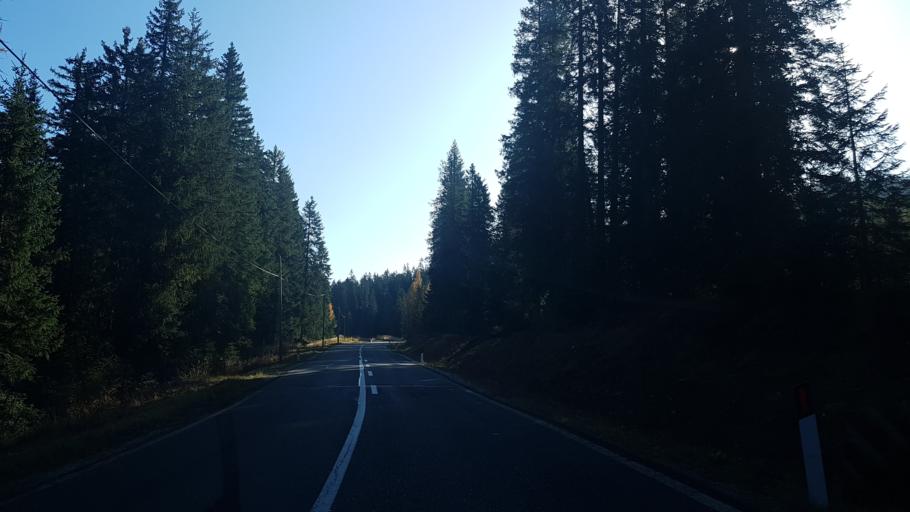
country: IT
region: Trentino-Alto Adige
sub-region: Bolzano
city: Sesto
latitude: 46.6606
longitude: 12.4045
